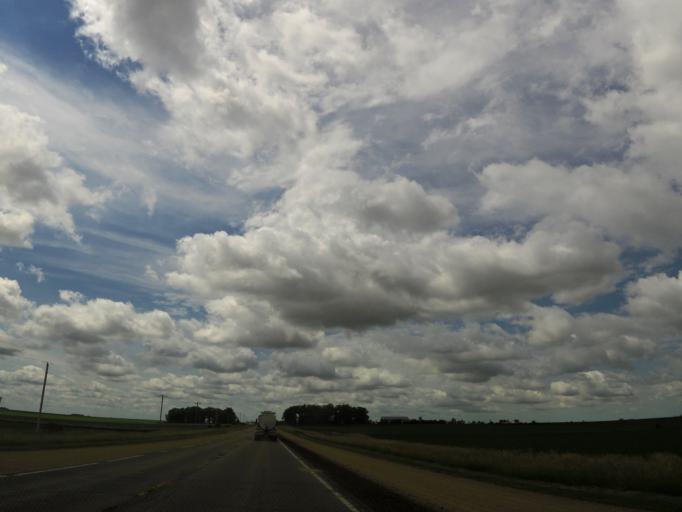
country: US
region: Iowa
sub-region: Howard County
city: Cresco
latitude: 43.3149
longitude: -92.2989
